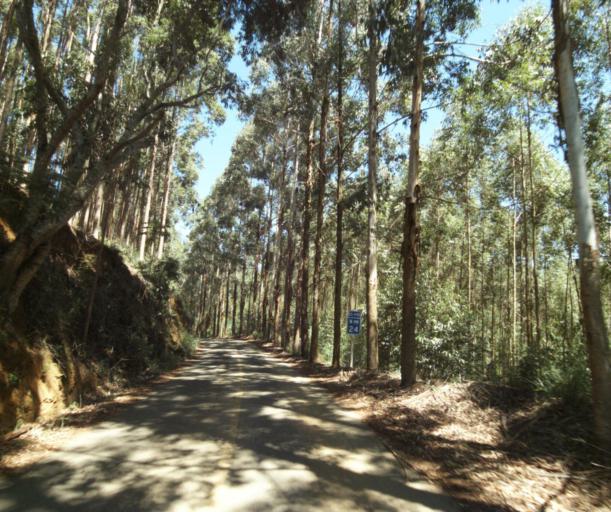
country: BR
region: Minas Gerais
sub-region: Espera Feliz
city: Espera Feliz
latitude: -20.6279
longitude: -41.8172
